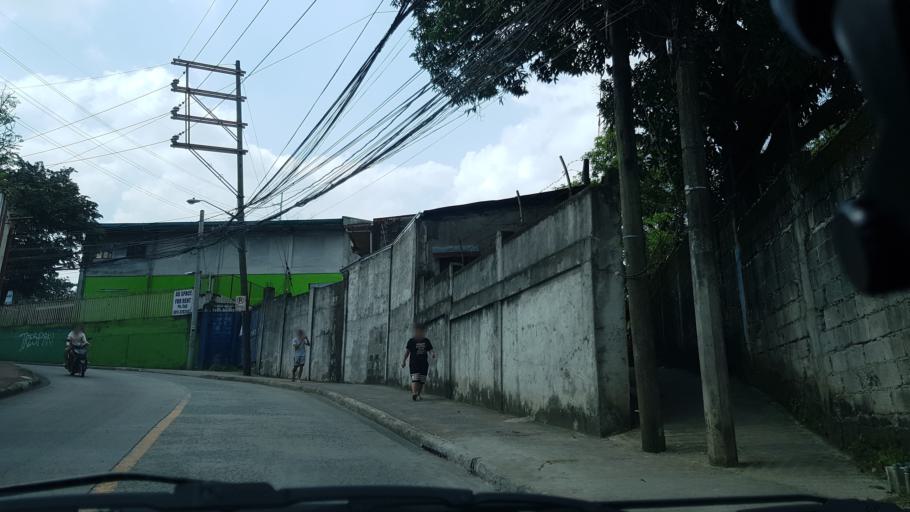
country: PH
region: Calabarzon
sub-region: Province of Rizal
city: Antipolo
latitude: 14.6581
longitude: 121.1271
